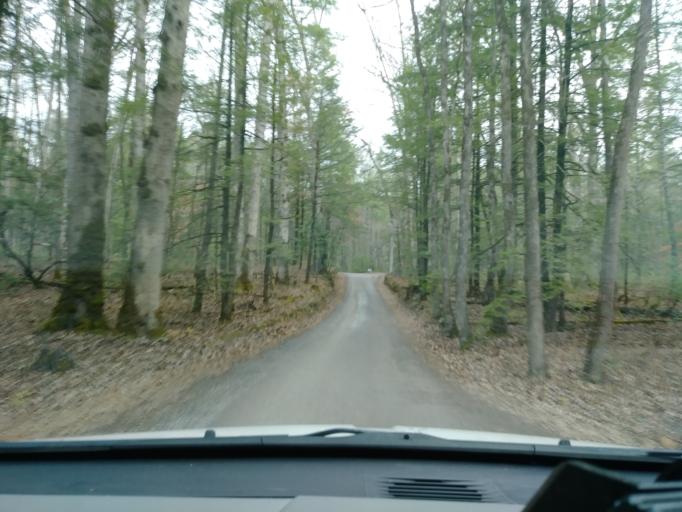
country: US
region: Tennessee
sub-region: Blount County
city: Wildwood
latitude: 35.6053
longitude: -83.8119
